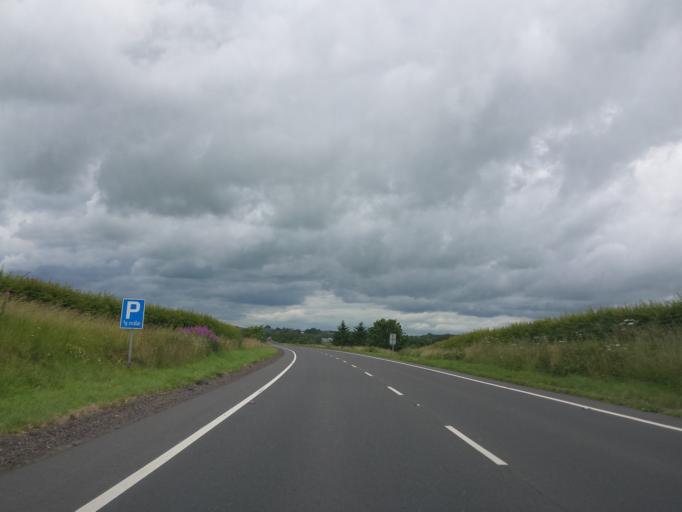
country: GB
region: Scotland
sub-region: Dumfries and Galloway
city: Castle Douglas
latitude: 54.9327
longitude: -3.9495
